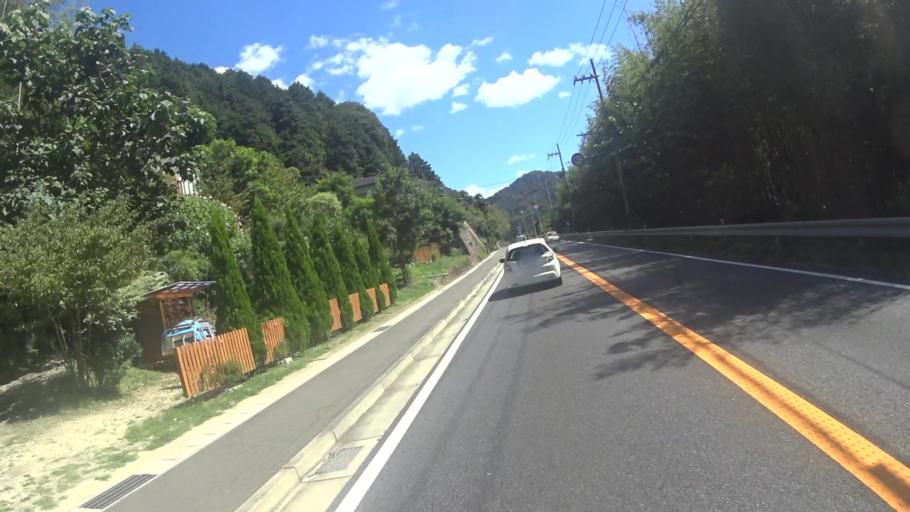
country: JP
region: Nara
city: Nara-shi
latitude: 34.7637
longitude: 135.9238
